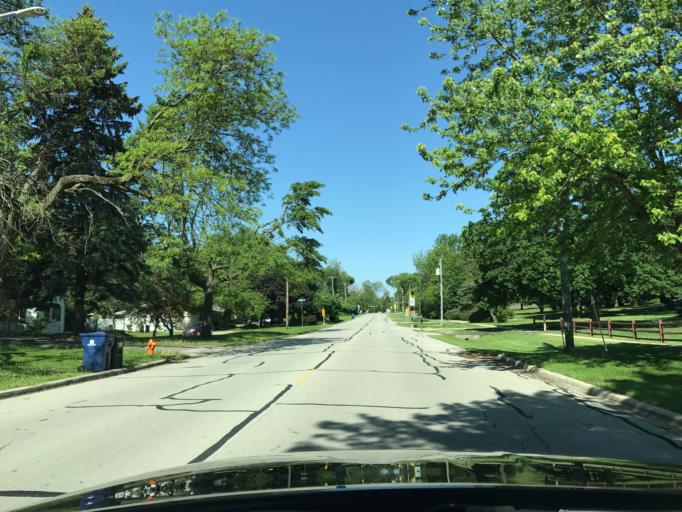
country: US
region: Illinois
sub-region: DuPage County
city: Naperville
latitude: 41.7940
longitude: -88.1486
